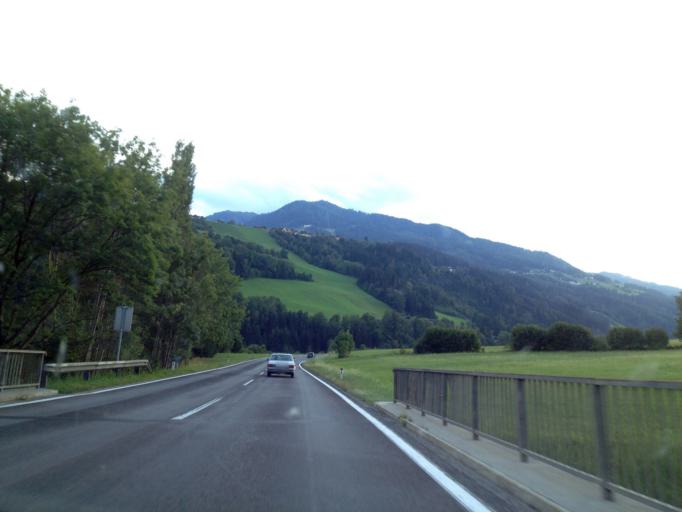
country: AT
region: Styria
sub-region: Politischer Bezirk Liezen
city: Schladming
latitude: 47.3942
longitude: 13.6732
